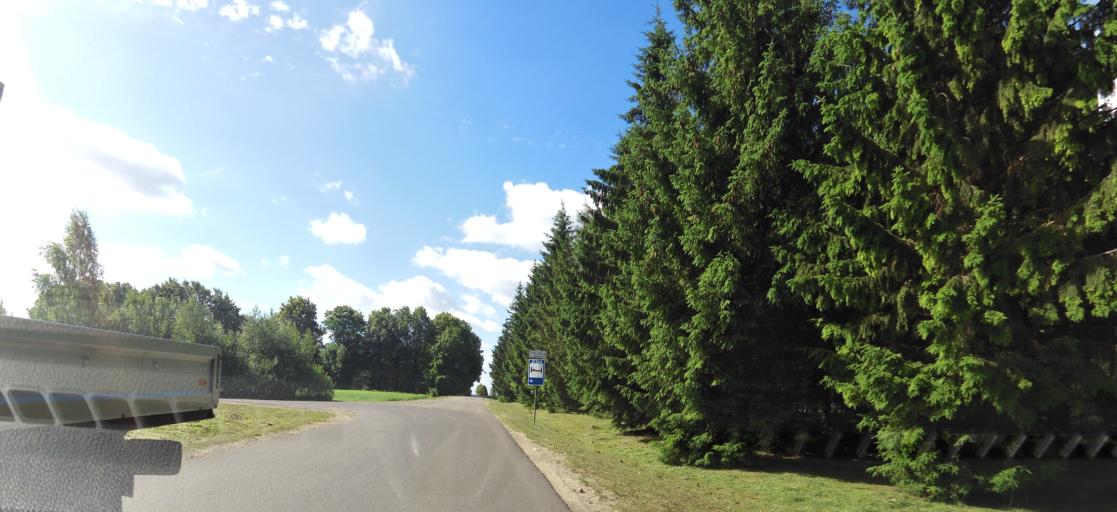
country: LT
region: Panevezys
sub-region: Birzai
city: Birzai
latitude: 56.1833
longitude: 24.7596
